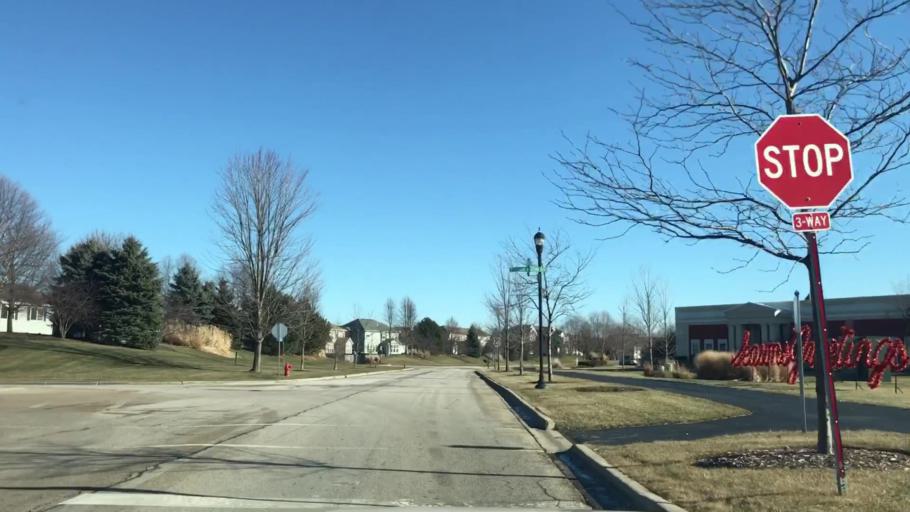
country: US
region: Illinois
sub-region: Kane County
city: Pingree Grove
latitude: 42.0857
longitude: -88.4364
